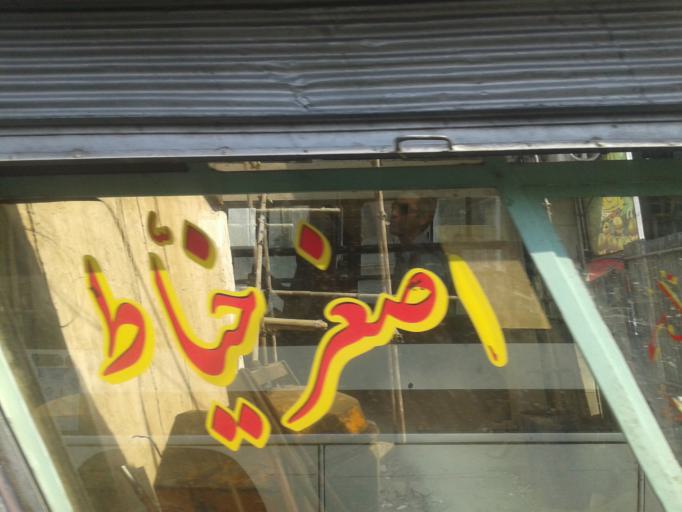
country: IR
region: Tehran
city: Eslamshahr
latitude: 35.6460
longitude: 51.3071
